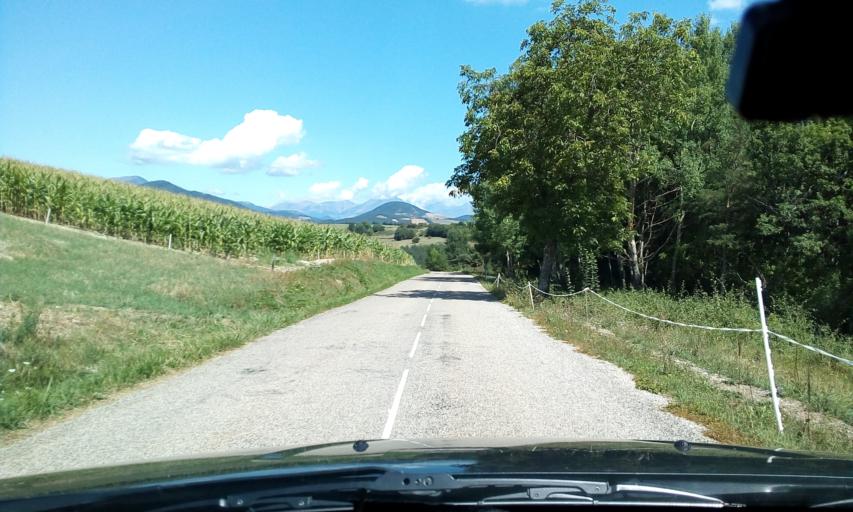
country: FR
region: Rhone-Alpes
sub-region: Departement de l'Isere
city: Mens
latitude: 44.7819
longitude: 5.6785
